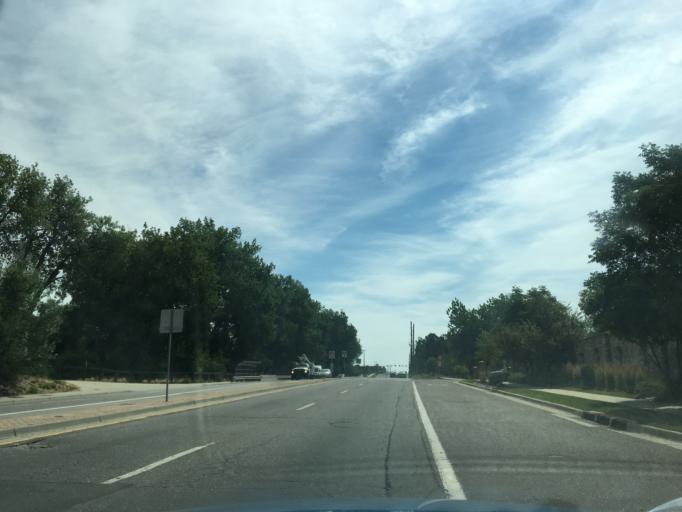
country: US
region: Colorado
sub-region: Arapahoe County
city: Glendale
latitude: 39.6747
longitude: -104.8818
